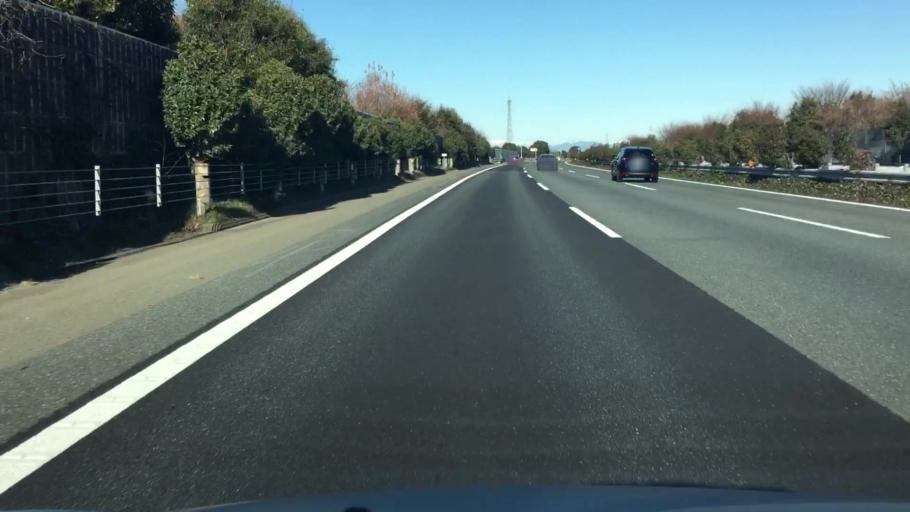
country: JP
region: Saitama
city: Yorii
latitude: 36.1391
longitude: 139.2266
